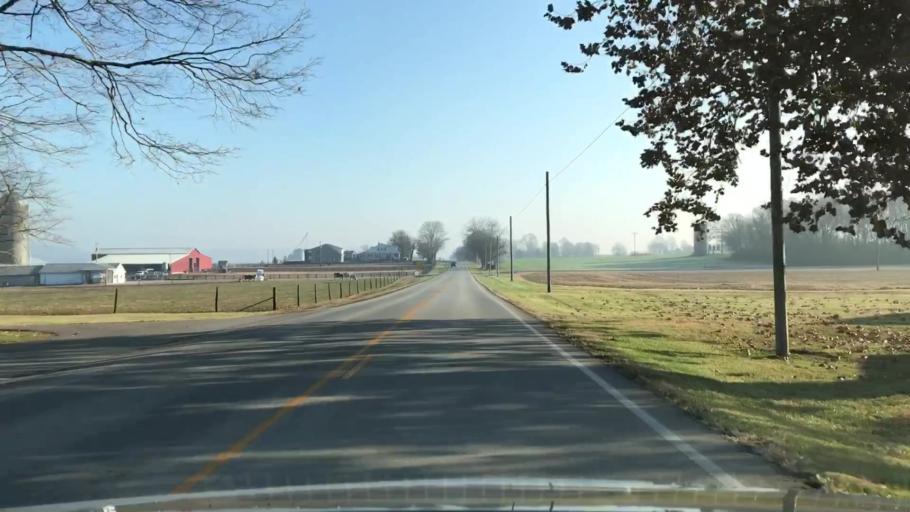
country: US
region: Kentucky
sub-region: Edmonson County
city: Brownsville
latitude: 37.0793
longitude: -86.2439
